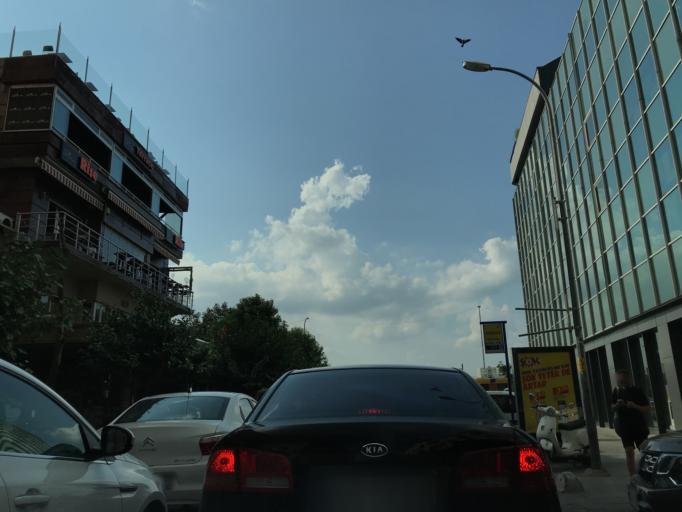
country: TR
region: Istanbul
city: UEskuedar
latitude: 40.9889
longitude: 29.0224
